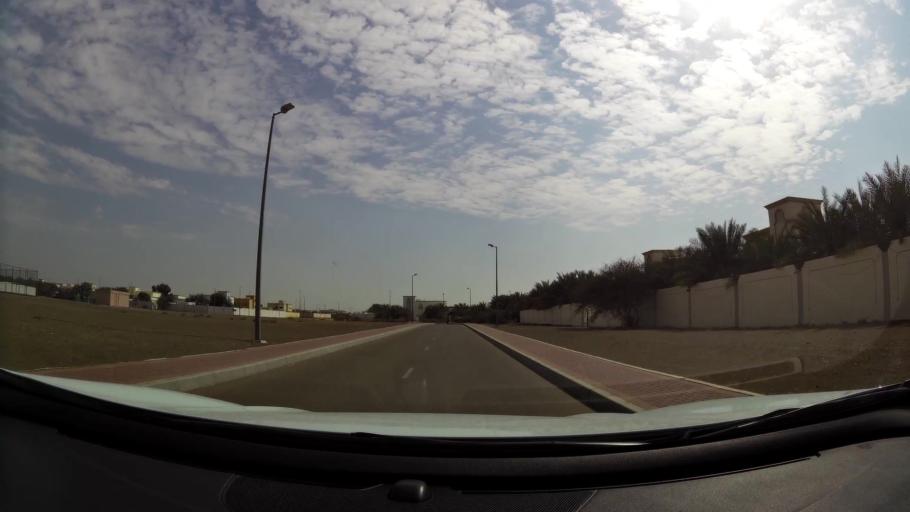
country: AE
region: Abu Dhabi
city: Al Ain
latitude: 24.0973
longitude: 55.9006
